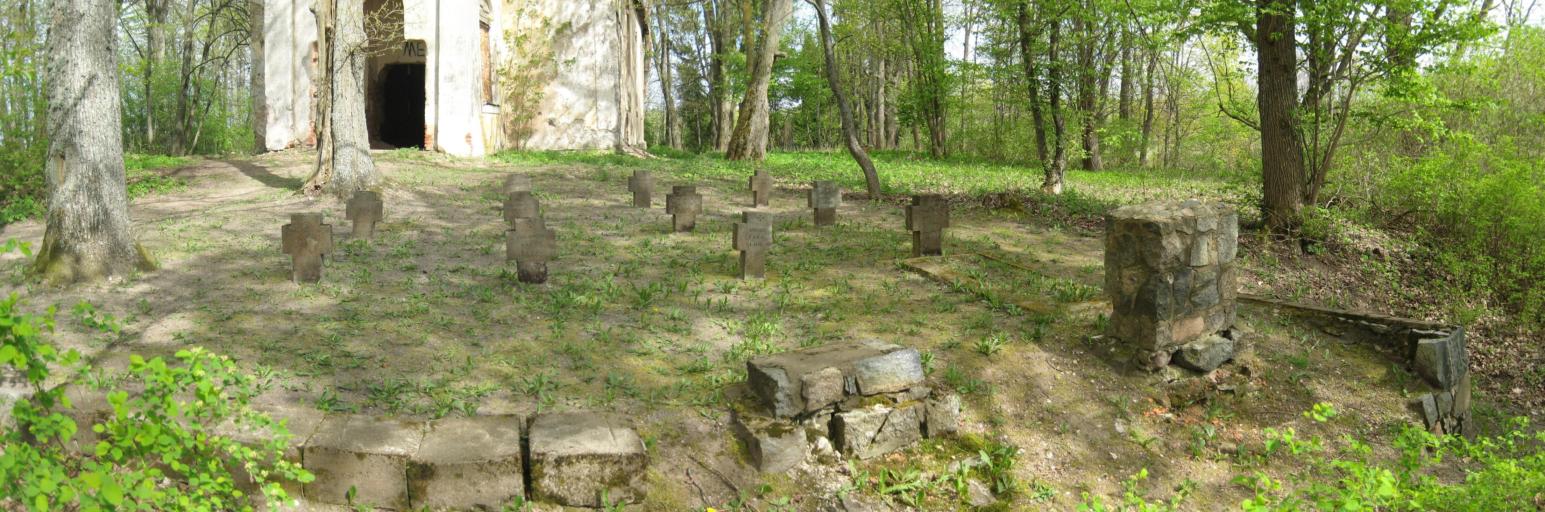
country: LT
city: Zarasai
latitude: 55.7473
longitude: 26.3111
